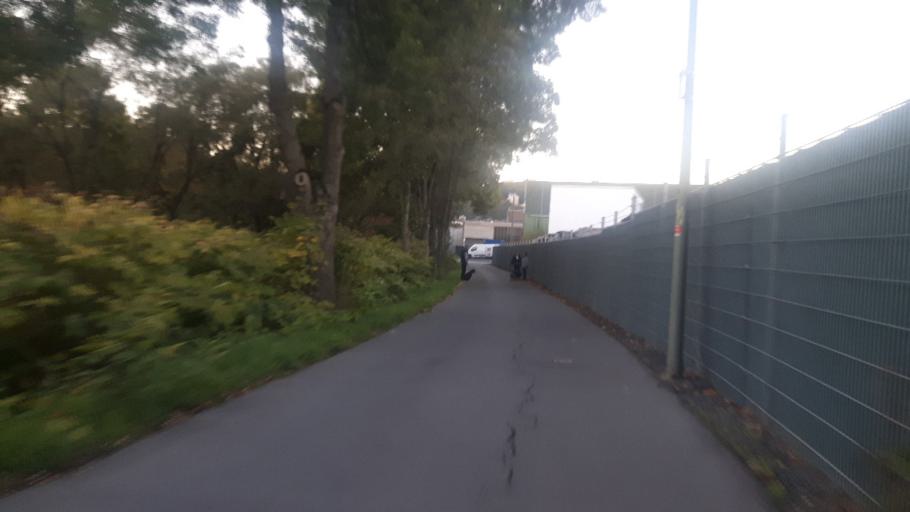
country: DE
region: North Rhine-Westphalia
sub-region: Regierungsbezirk Arnsberg
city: Siegen
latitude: 50.8626
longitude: 8.0086
